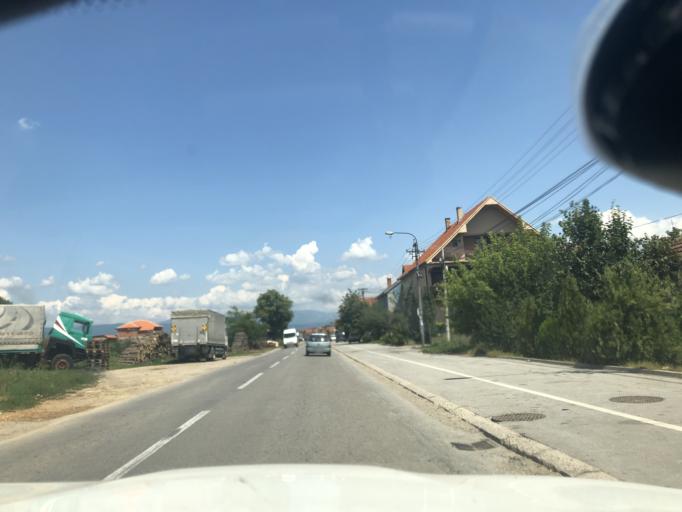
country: RS
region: Central Serbia
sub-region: Jablanicki Okrug
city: Leskovac
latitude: 42.9824
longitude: 21.9135
